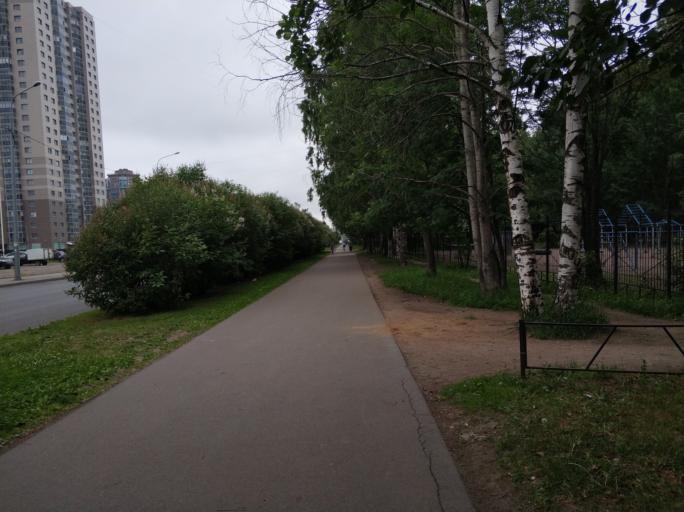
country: RU
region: St.-Petersburg
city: Grazhdanka
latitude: 60.0345
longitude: 30.4094
